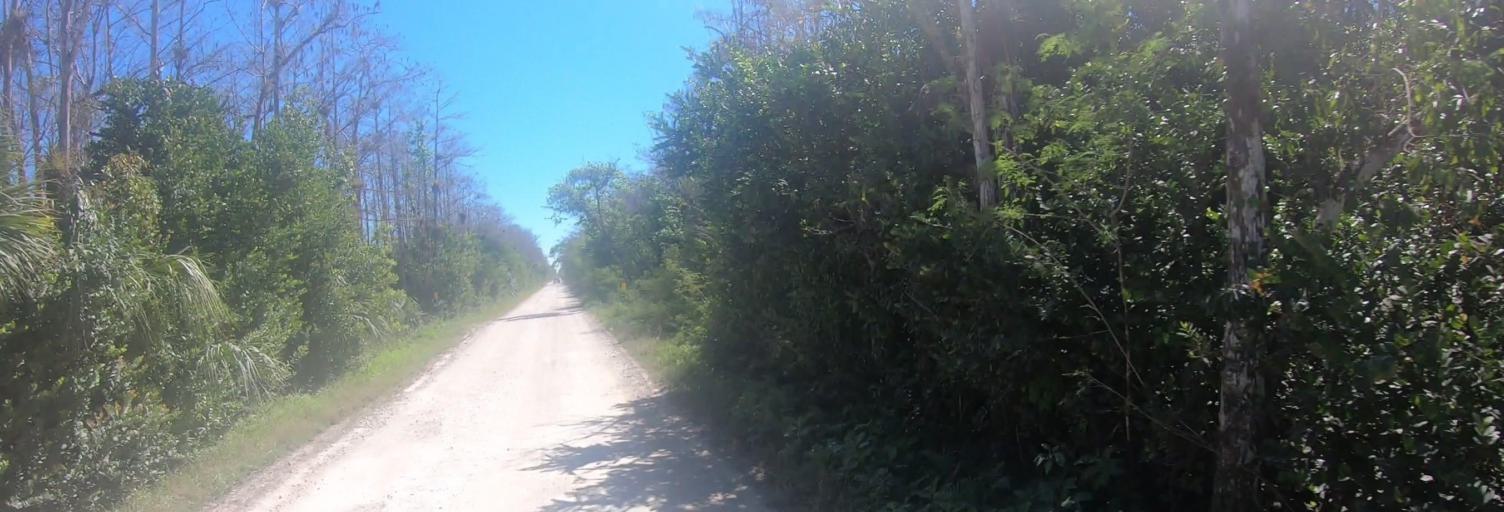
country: US
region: Florida
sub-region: Miami-Dade County
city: The Hammocks
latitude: 25.7553
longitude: -80.9806
